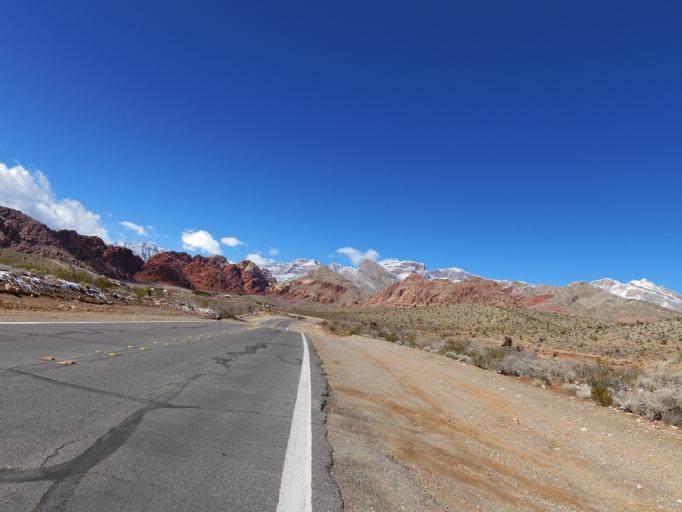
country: US
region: Nevada
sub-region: Clark County
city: Summerlin South
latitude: 36.1443
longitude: -115.4027
